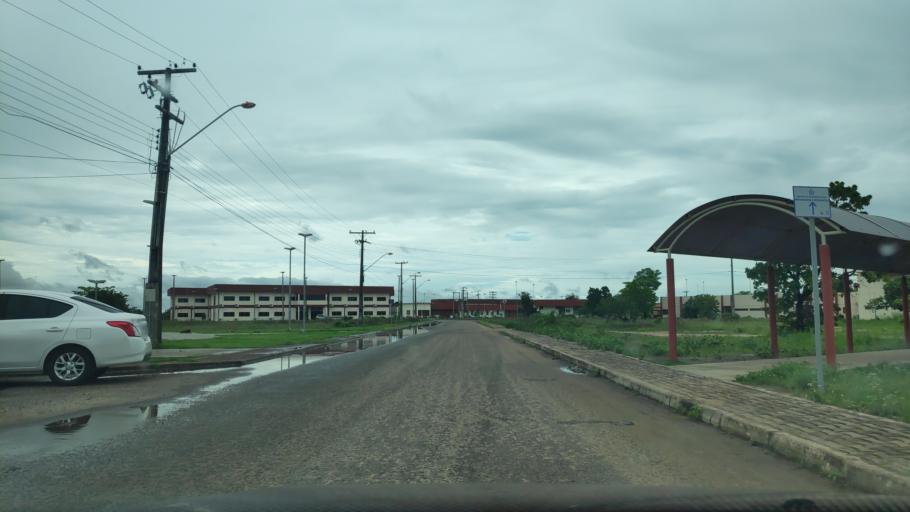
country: BR
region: Roraima
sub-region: Boa Vista
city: Boa Vista
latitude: 2.8331
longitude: -60.6980
